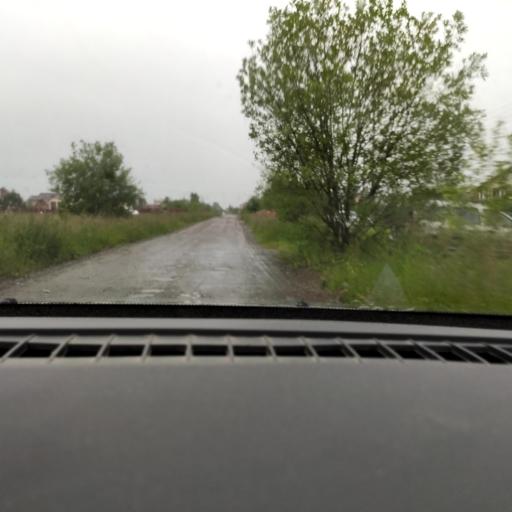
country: RU
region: Perm
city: Perm
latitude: 58.0423
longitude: 56.3734
